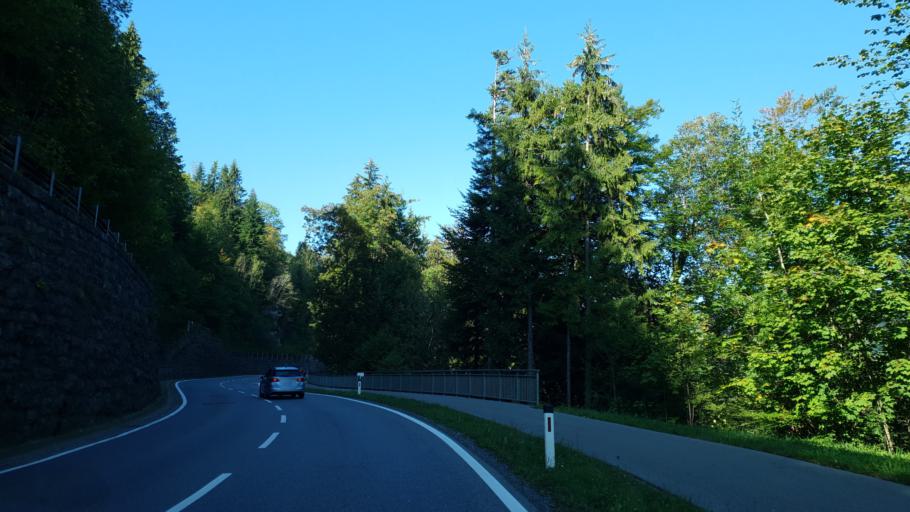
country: AT
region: Vorarlberg
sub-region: Politischer Bezirk Bregenz
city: Andelsbuch
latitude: 47.4012
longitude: 9.8752
